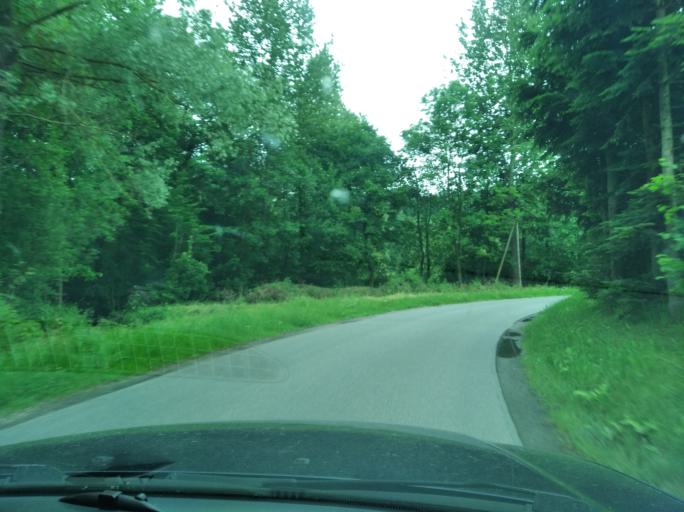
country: PL
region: Subcarpathian Voivodeship
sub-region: Powiat przemyski
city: Nienadowa
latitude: 49.8432
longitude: 22.4144
